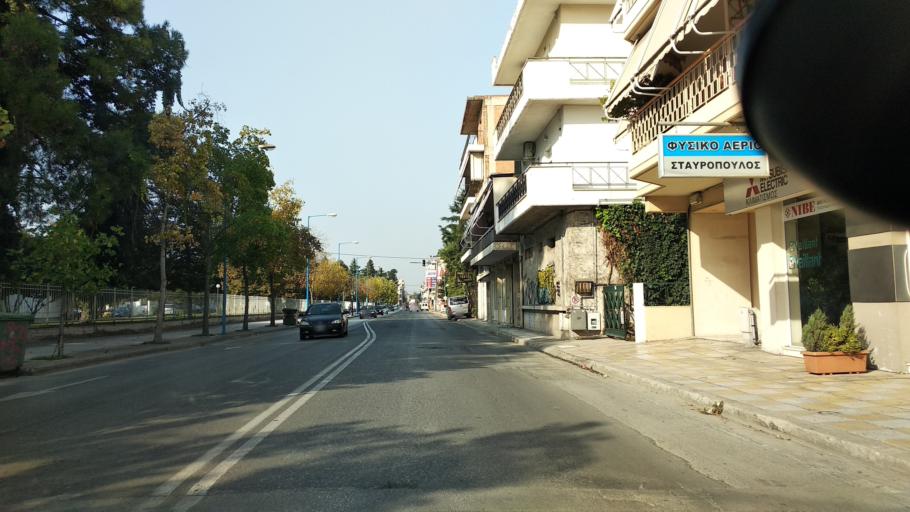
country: GR
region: Thessaly
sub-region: Nomos Larisis
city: Larisa
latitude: 39.6328
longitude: 22.4033
